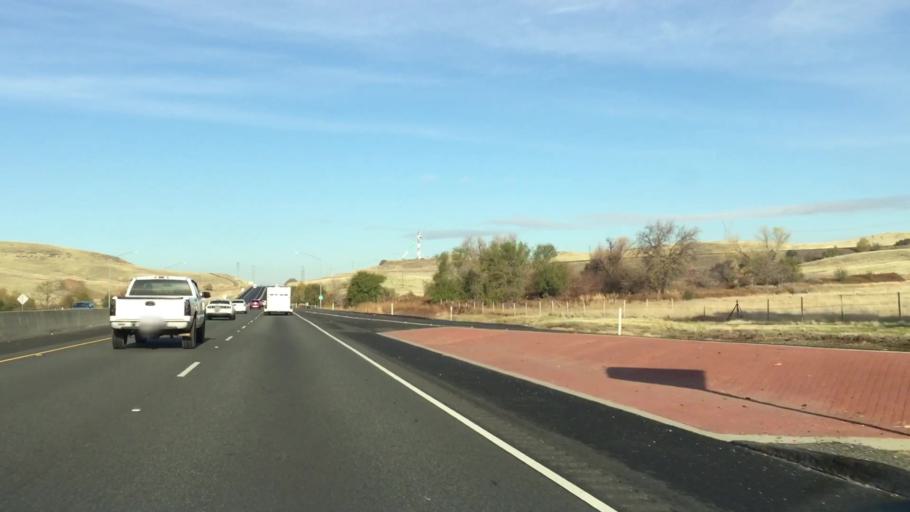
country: US
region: California
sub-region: Butte County
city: Thermalito
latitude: 39.5361
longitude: -121.5836
